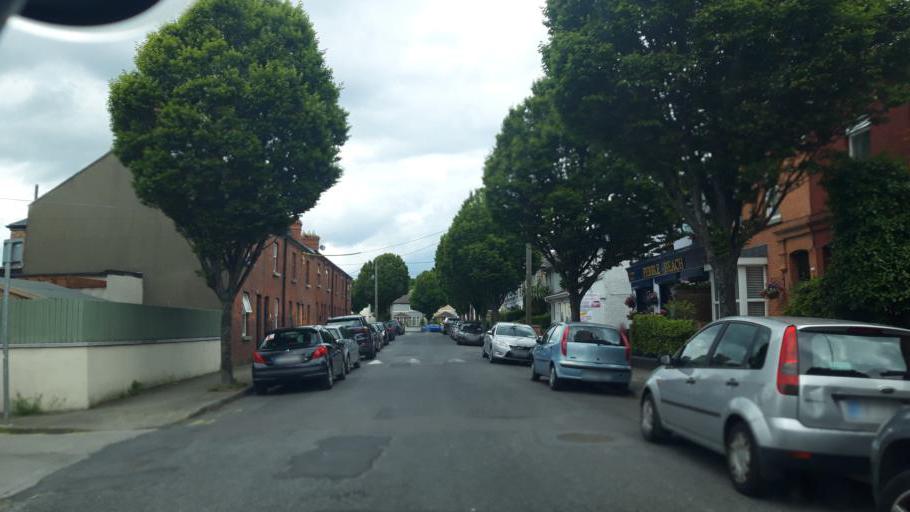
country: IE
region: Leinster
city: Dollymount
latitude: 53.3593
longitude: -6.1899
